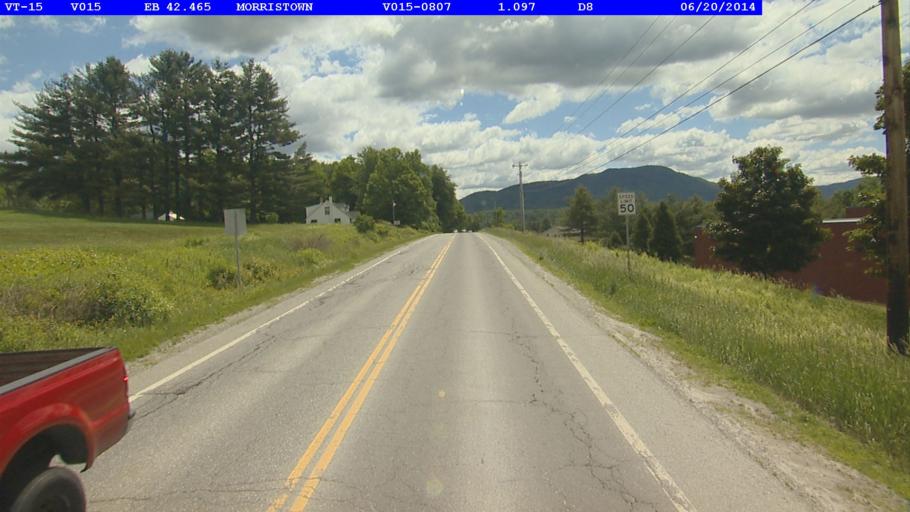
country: US
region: Vermont
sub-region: Lamoille County
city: Morrisville
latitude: 44.5736
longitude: -72.5890
